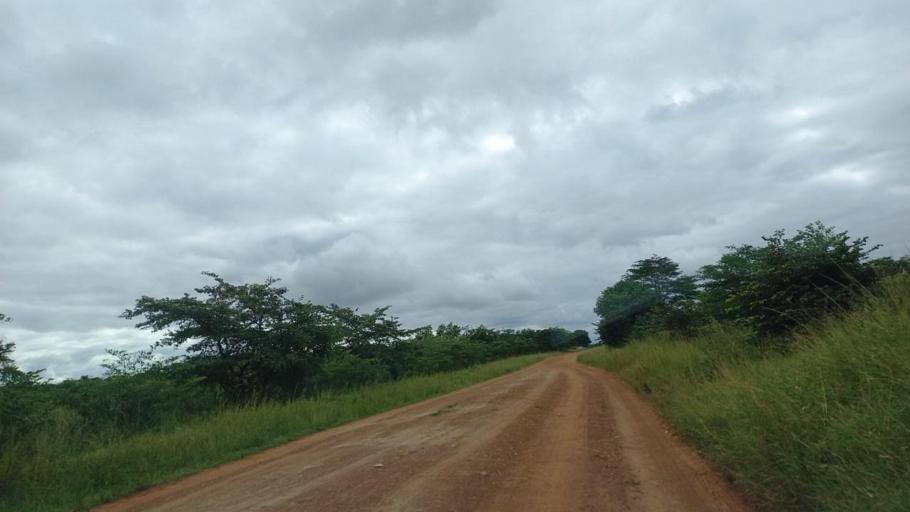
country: ZM
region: Lusaka
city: Chongwe
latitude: -15.4568
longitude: 28.8740
